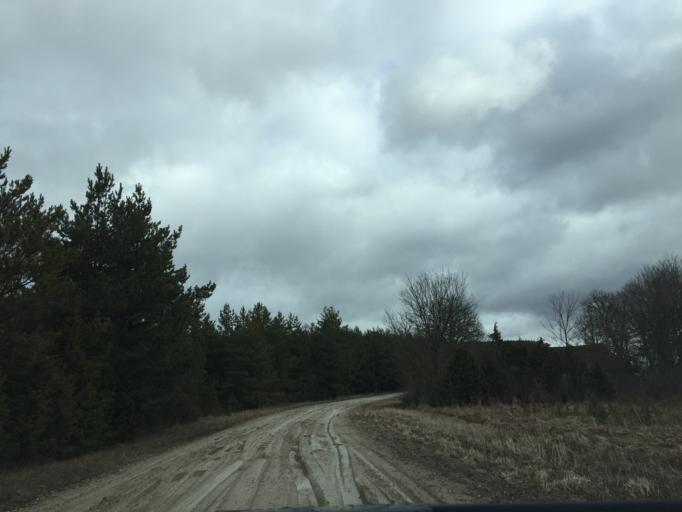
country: EE
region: Laeaene
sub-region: Ridala Parish
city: Uuemoisa
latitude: 58.6876
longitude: 23.5485
